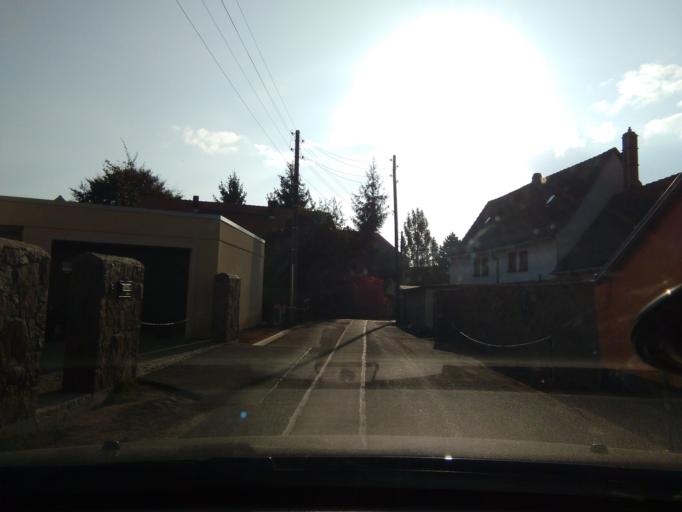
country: DE
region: Saxony
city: Niederau
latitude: 51.1379
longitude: 13.5176
